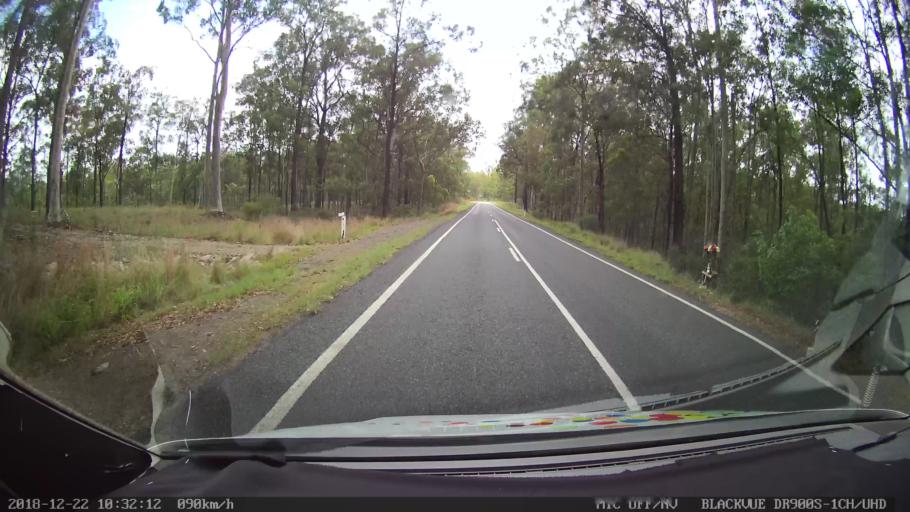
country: AU
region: New South Wales
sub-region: Clarence Valley
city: South Grafton
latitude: -29.6213
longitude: 152.6379
